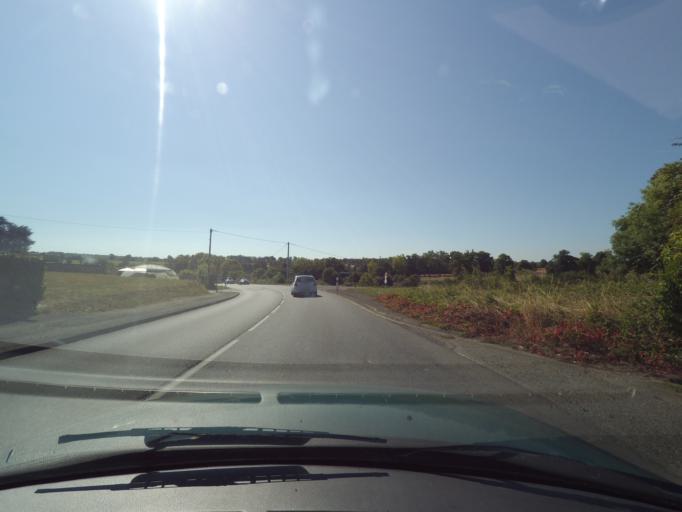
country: FR
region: Limousin
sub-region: Departement de la Haute-Vienne
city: Bussiere-Poitevine
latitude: 46.1668
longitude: 0.9543
